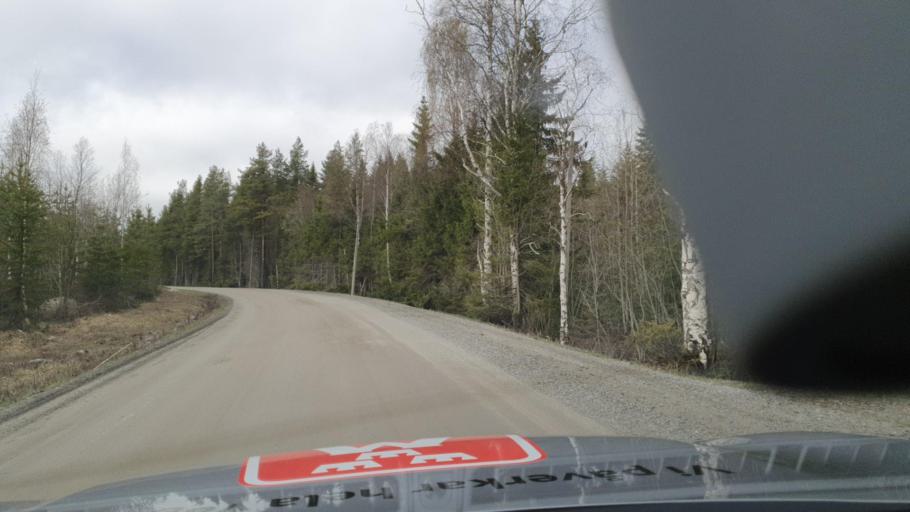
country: SE
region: Vaesterbotten
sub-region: Bjurholms Kommun
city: Bjurholm
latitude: 63.6834
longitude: 18.9798
